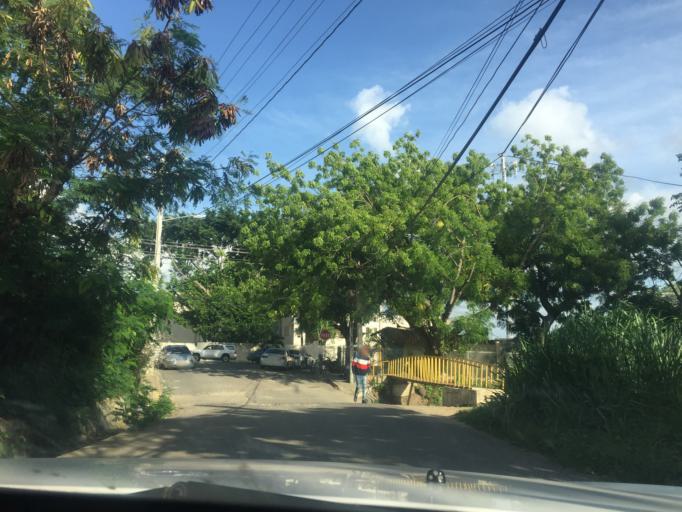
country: DO
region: Santiago
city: Tamboril
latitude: 19.4810
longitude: -70.6377
